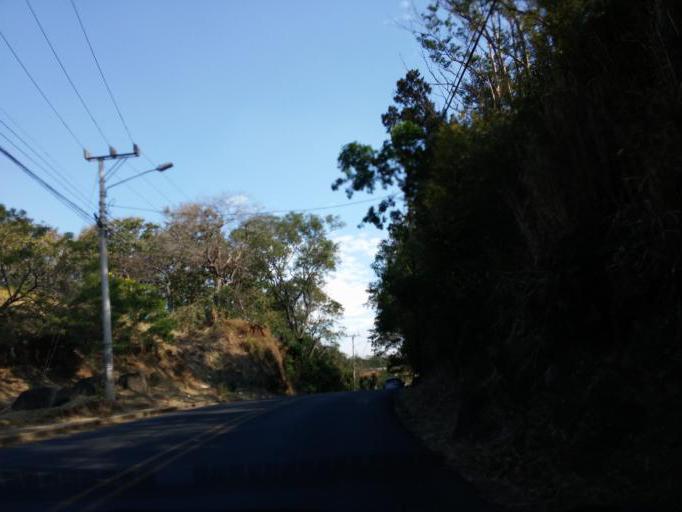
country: CR
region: Heredia
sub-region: Canton de Belen
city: San Antonio
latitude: 9.9857
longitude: -84.1929
